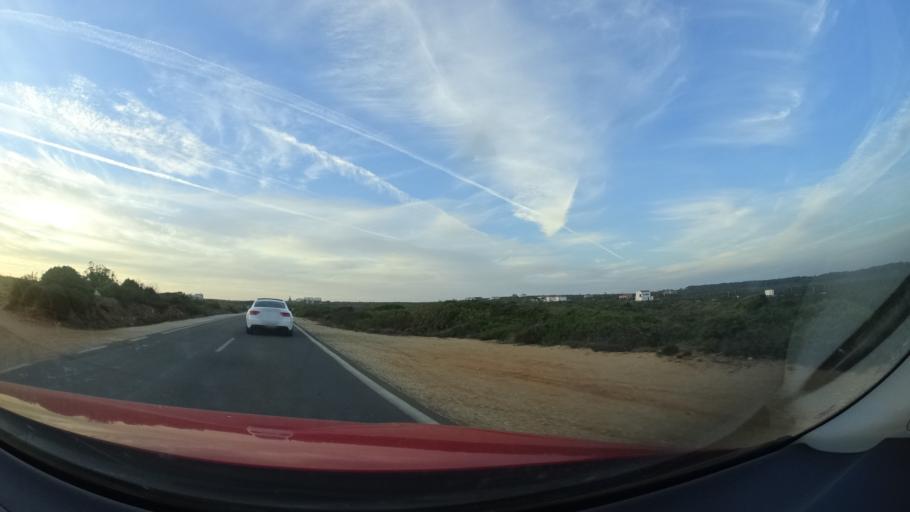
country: PT
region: Faro
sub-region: Vila do Bispo
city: Sagres
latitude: 37.0201
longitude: -8.9584
